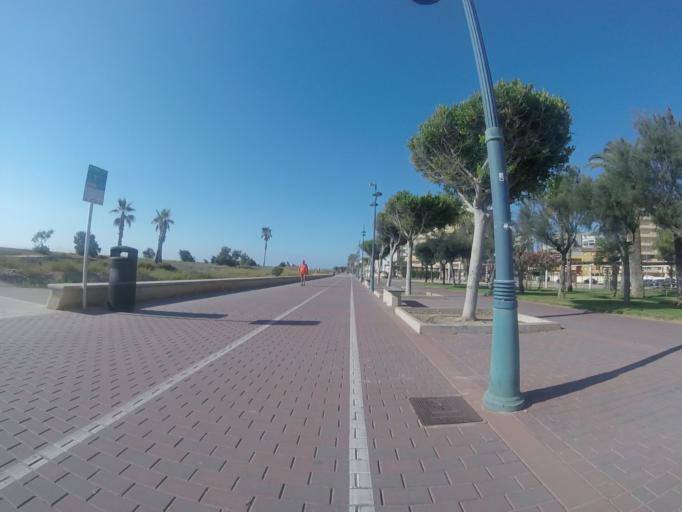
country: ES
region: Valencia
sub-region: Provincia de Castello
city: Peniscola
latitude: 40.3822
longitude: 0.4087
